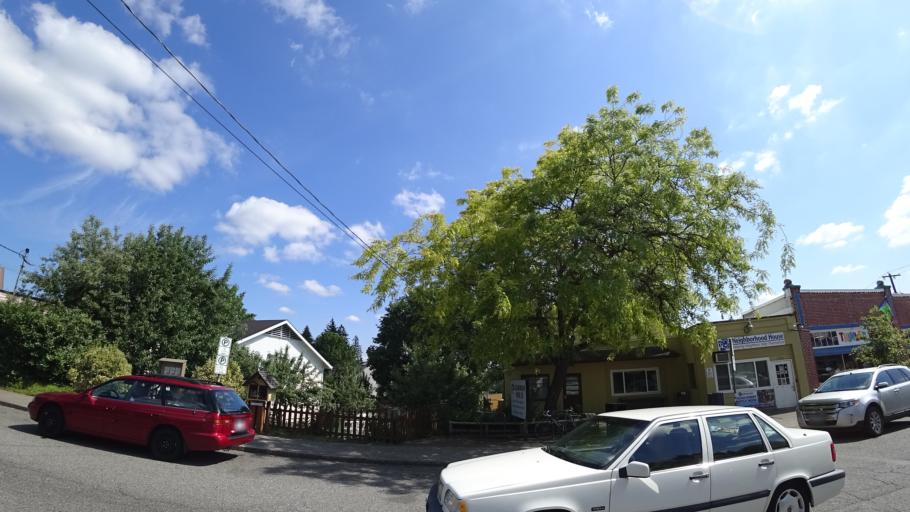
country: US
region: Oregon
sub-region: Washington County
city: Garden Home-Whitford
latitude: 45.4682
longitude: -122.7124
